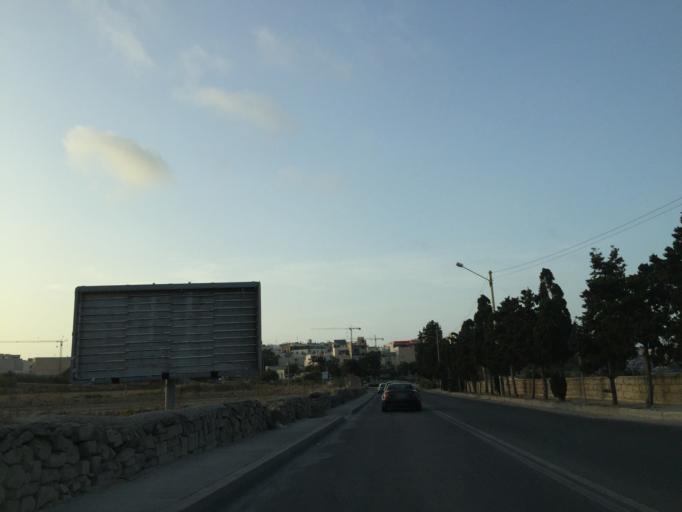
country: MT
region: Saint Paul's Bay
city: San Pawl il-Bahar
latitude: 35.9423
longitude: 14.4115
